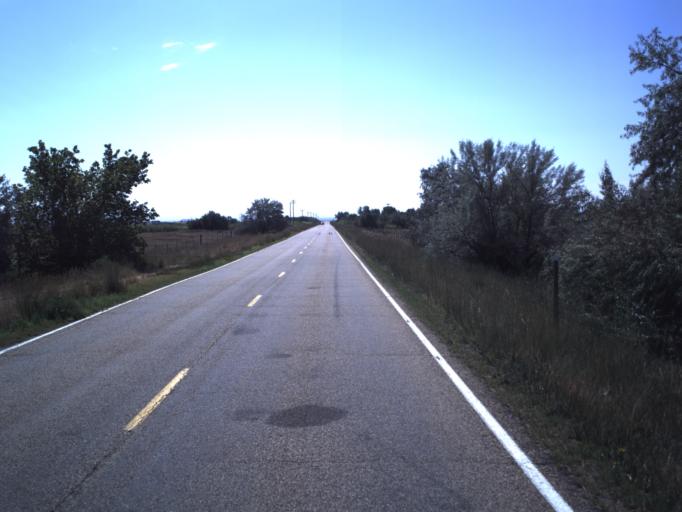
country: US
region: Utah
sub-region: Duchesne County
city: Duchesne
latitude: 40.3209
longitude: -110.2591
